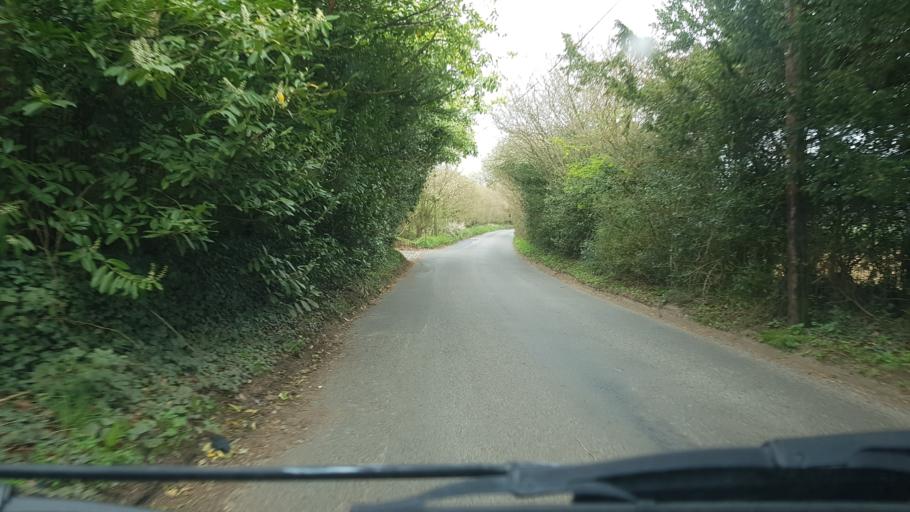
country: GB
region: England
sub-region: Surrey
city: Cranleigh
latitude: 51.1926
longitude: -0.4631
